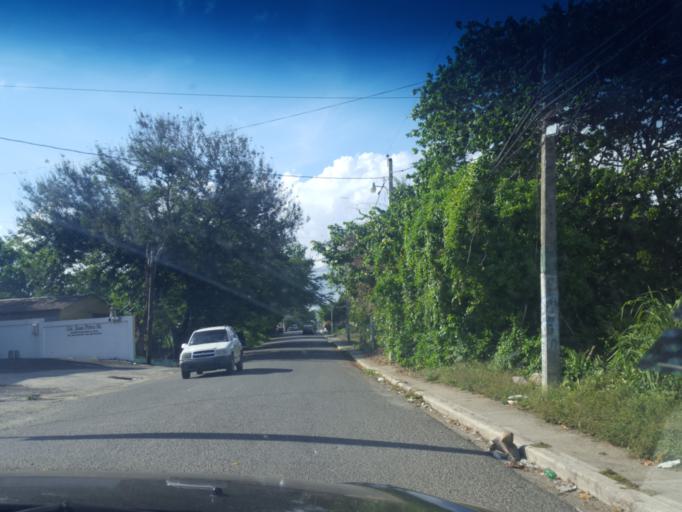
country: DO
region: La Vega
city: Rio Verde Arriba
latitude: 19.3629
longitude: -70.6050
